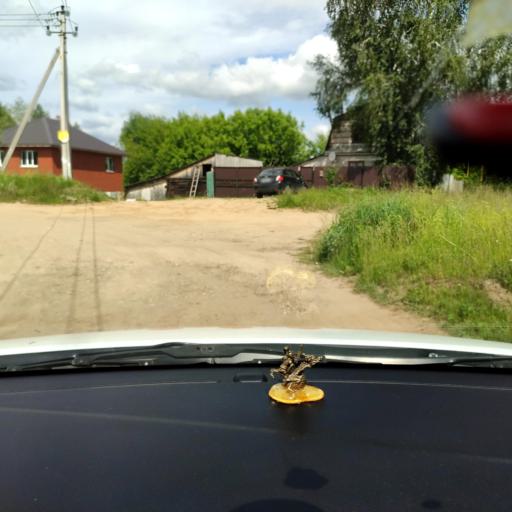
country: RU
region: Tatarstan
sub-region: Zelenodol'skiy Rayon
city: Vasil'yevo
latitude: 55.8371
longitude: 48.7206
